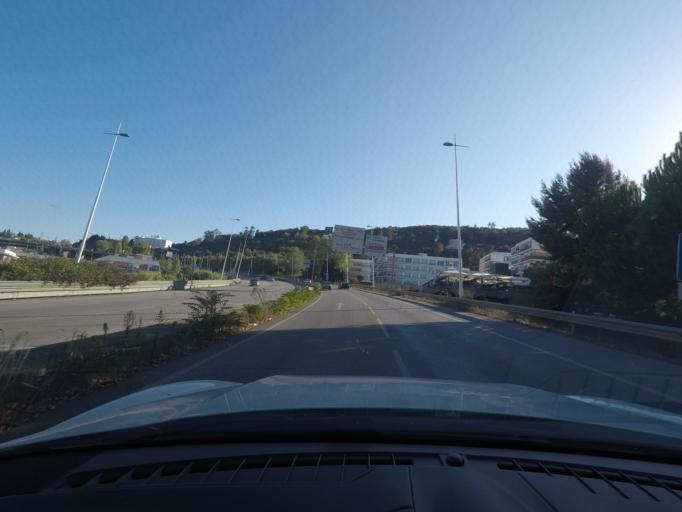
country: PT
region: Coimbra
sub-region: Coimbra
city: Coimbra
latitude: 40.1952
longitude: -8.4321
